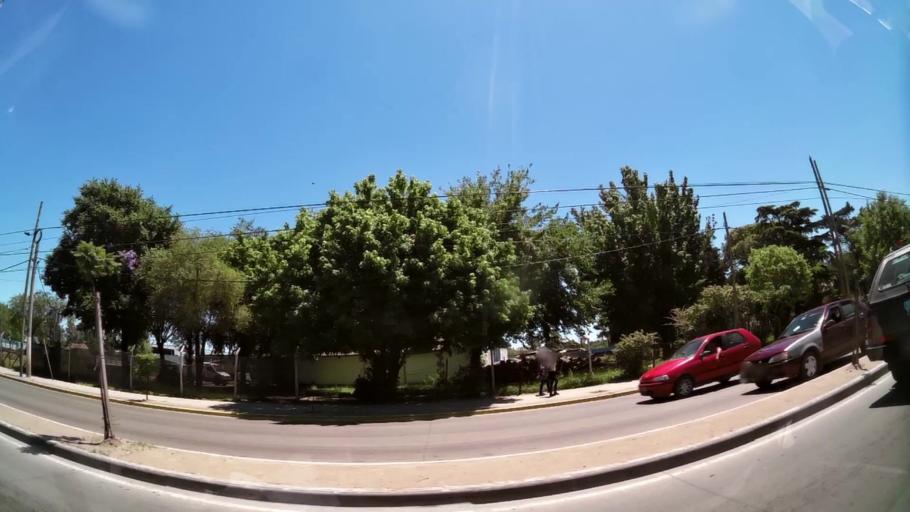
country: AR
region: Buenos Aires
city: Hurlingham
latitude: -34.4986
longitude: -58.7097
